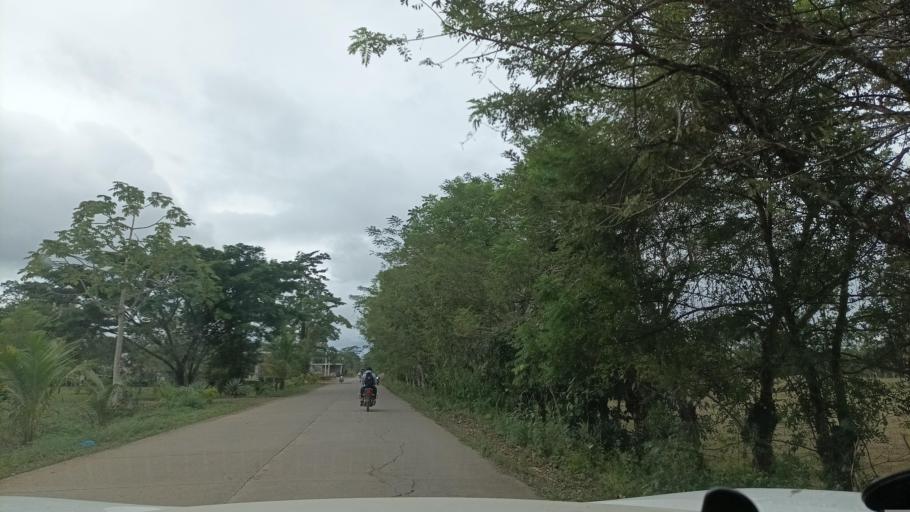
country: MX
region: Veracruz
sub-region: Uxpanapa
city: Poblado 10
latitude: 17.2775
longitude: -94.4651
